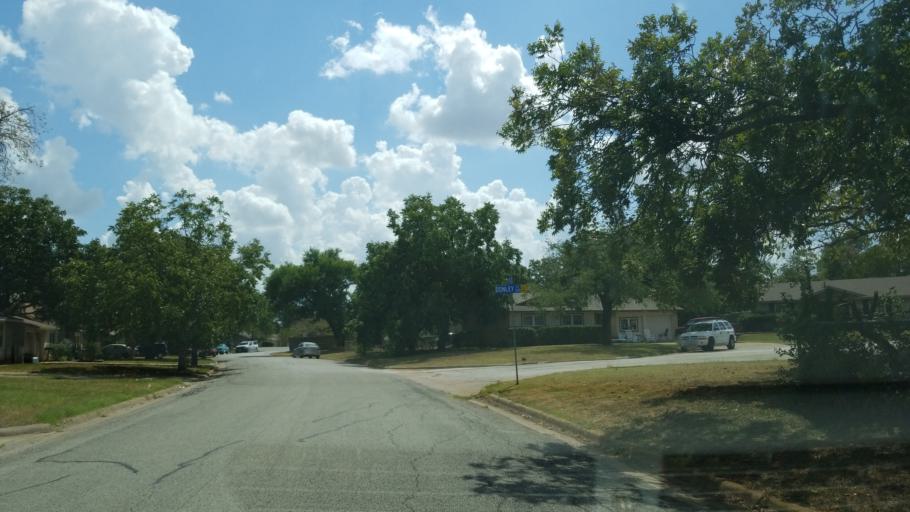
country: US
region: Texas
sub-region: Tarrant County
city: Euless
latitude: 32.8531
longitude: -97.0940
